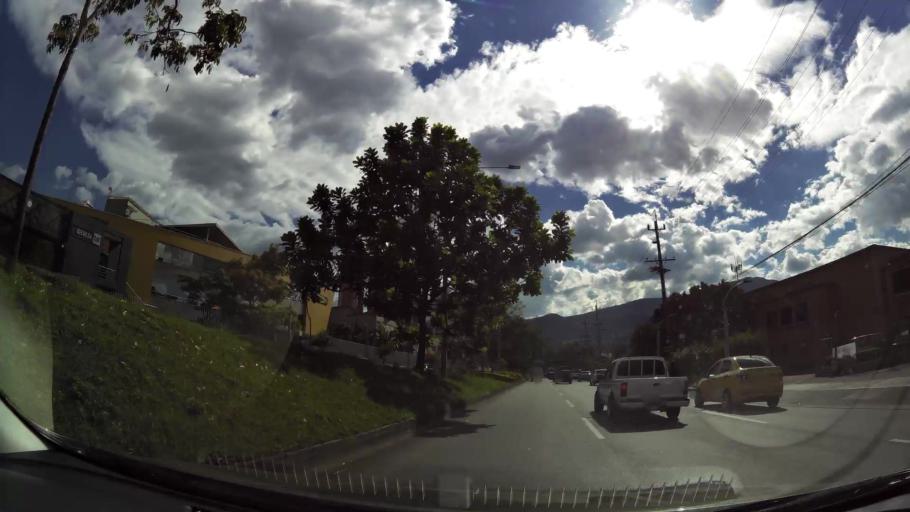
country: CO
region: Antioquia
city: Sabaneta
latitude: 6.1592
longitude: -75.6075
